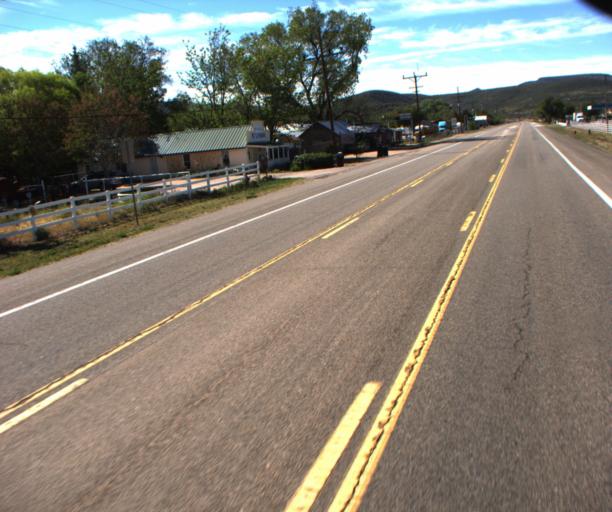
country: US
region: Arizona
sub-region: Yavapai County
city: Congress
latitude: 34.2698
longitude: -112.7273
